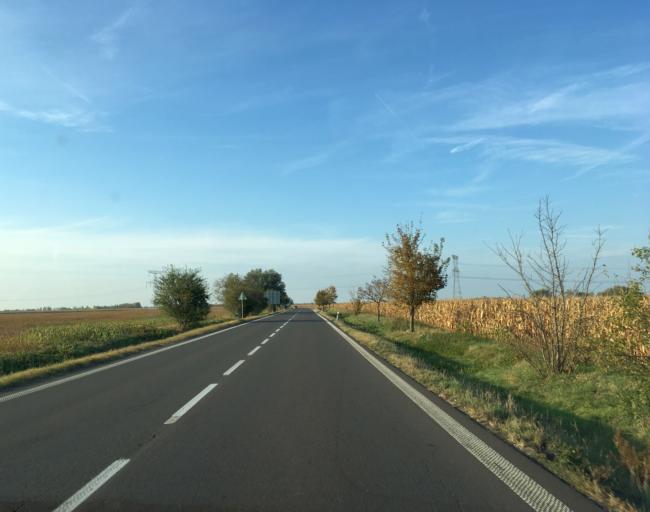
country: SK
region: Nitriansky
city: Surany
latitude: 48.0635
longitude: 18.0985
